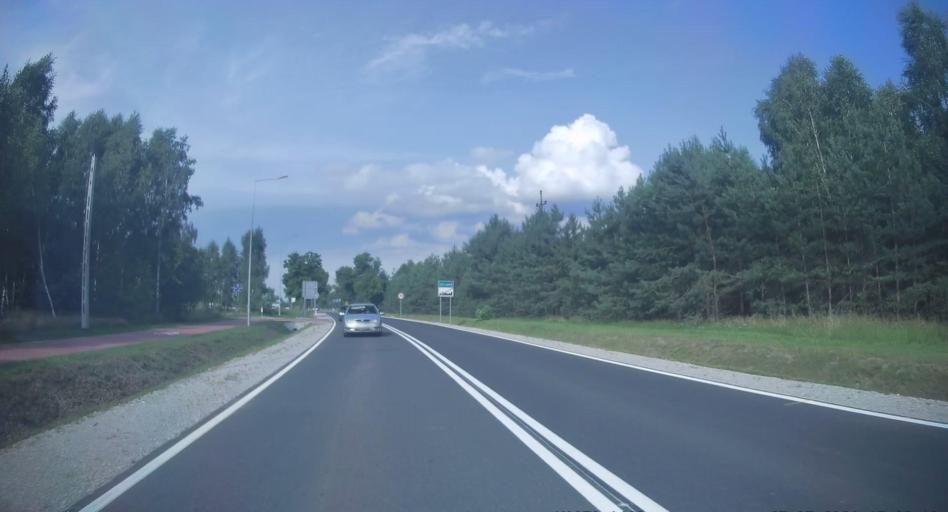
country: PL
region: Lodz Voivodeship
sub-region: Powiat tomaszowski
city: Inowlodz
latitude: 51.5576
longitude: 20.2591
